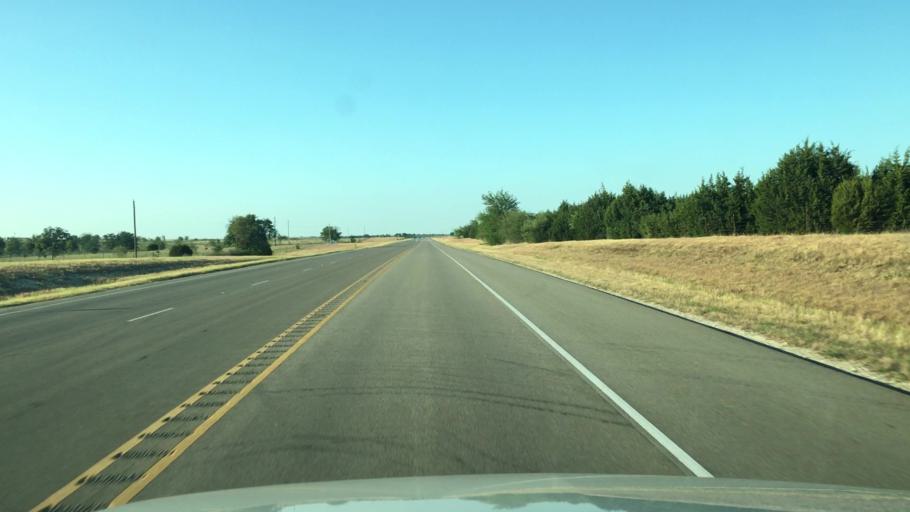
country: US
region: Texas
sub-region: Hamilton County
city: Hamilton
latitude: 31.6232
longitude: -98.1559
